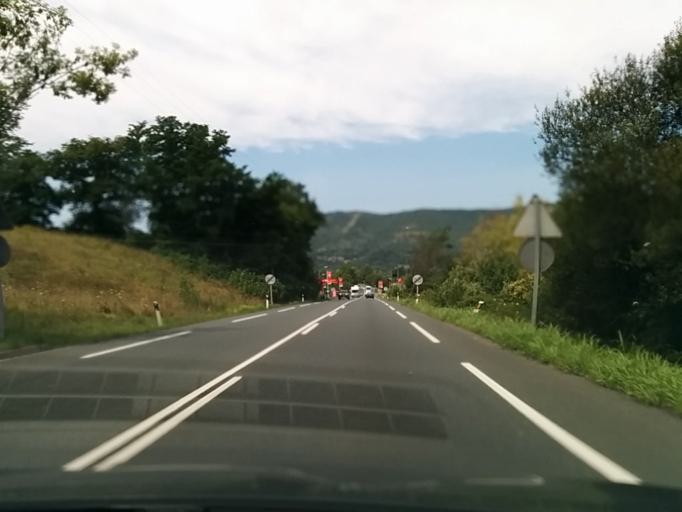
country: ES
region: Basque Country
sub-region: Provincia de Guipuzcoa
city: Irun
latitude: 43.3470
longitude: -1.8051
